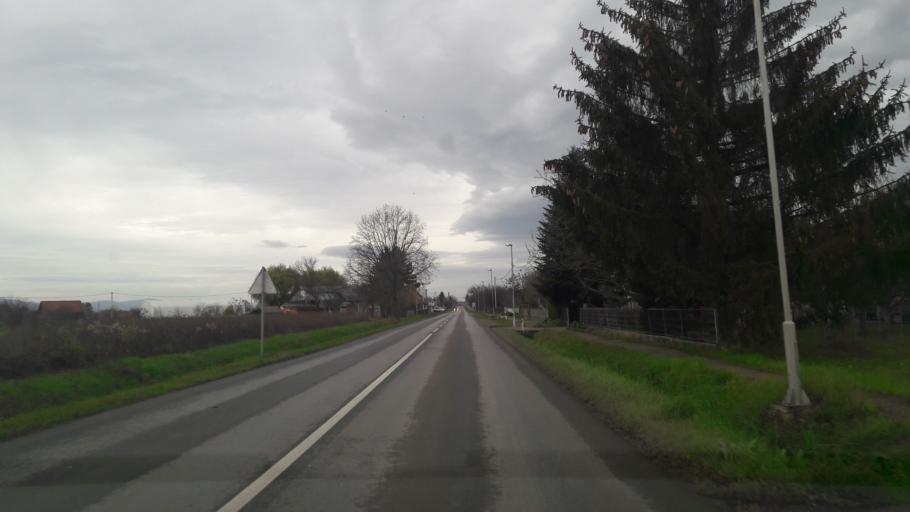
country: HR
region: Osjecko-Baranjska
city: Velimirovac
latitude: 45.5356
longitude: 18.0764
